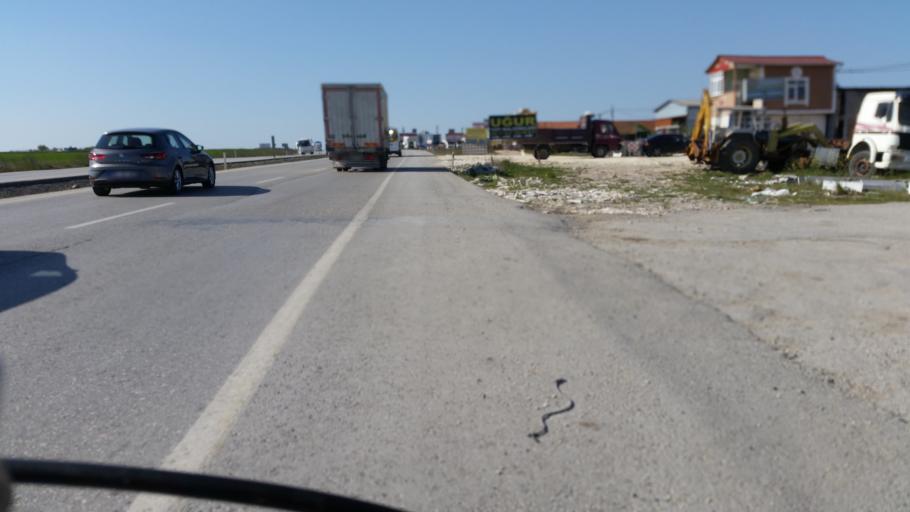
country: TR
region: Tekirdag
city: Cerkezkoey
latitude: 41.3385
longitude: 27.9666
